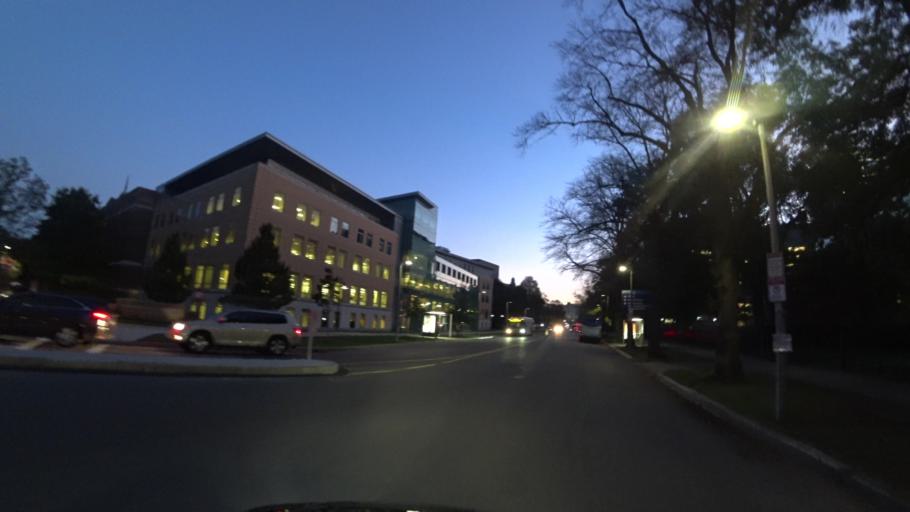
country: US
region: Massachusetts
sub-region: Norfolk County
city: Brookline
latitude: 42.3405
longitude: -71.1010
